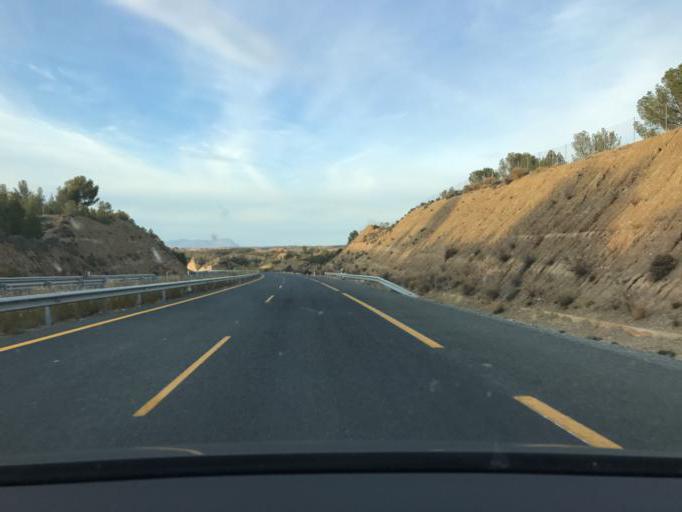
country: ES
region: Andalusia
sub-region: Provincia de Granada
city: Guadix
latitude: 37.2761
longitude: -3.0955
